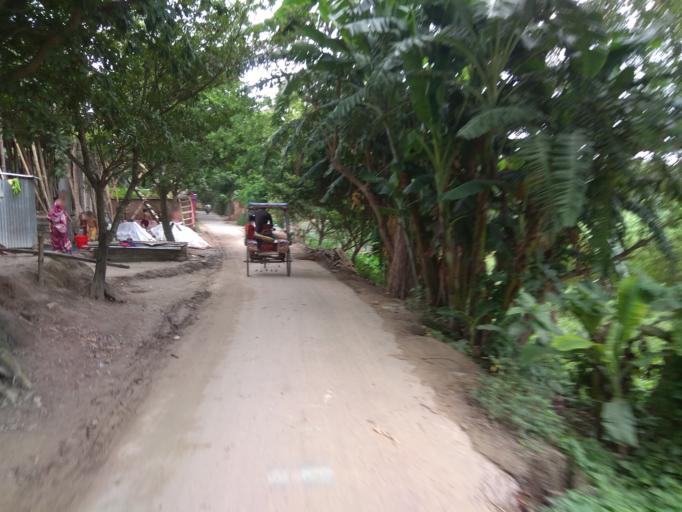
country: BD
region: Dhaka
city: Dohar
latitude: 23.4839
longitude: 90.0028
